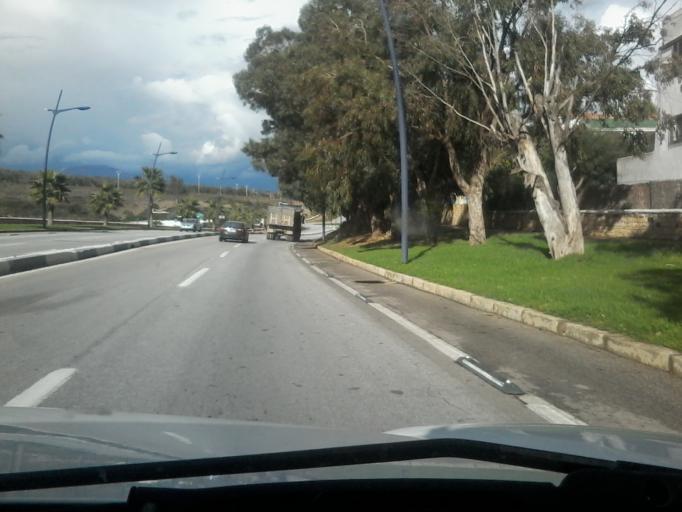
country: ES
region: Ceuta
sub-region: Ceuta
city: Ceuta
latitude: 35.7614
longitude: -5.3486
